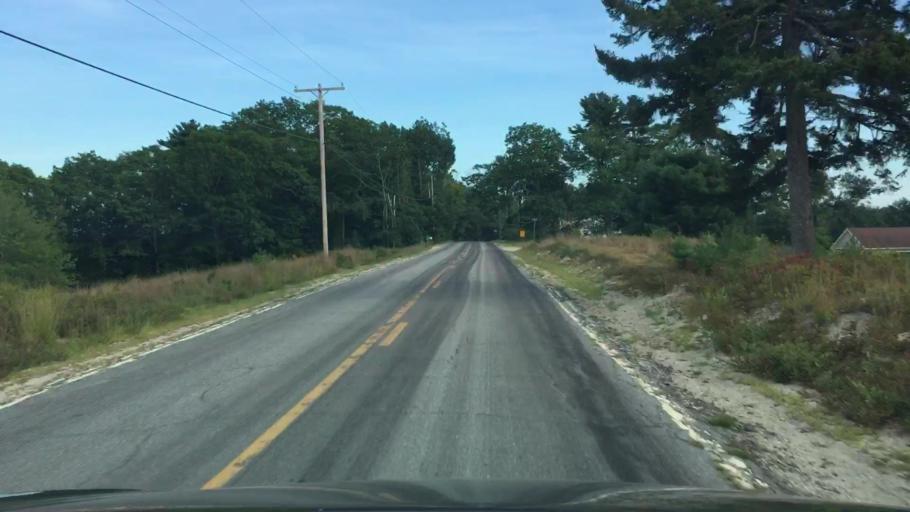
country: US
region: Maine
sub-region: Hancock County
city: Surry
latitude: 44.5135
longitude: -68.6016
